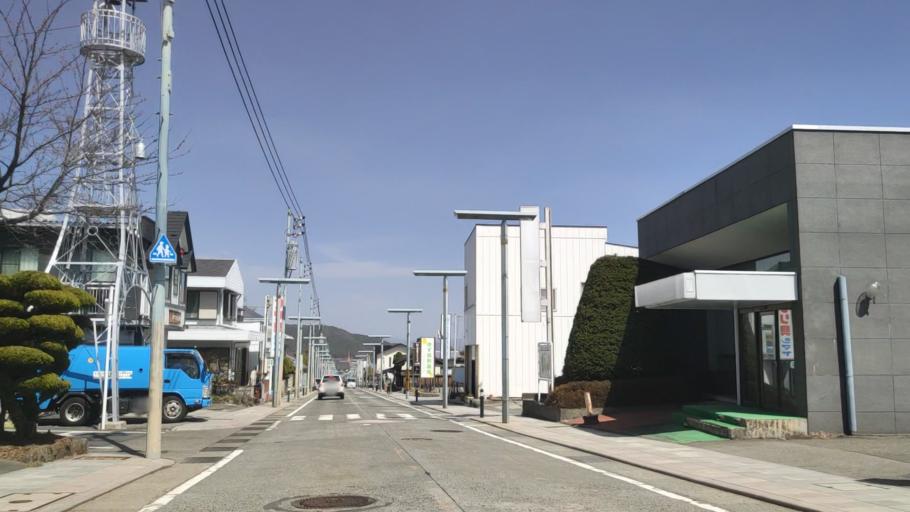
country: JP
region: Yamanashi
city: Fujikawaguchiko
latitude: 35.4781
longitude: 138.7941
